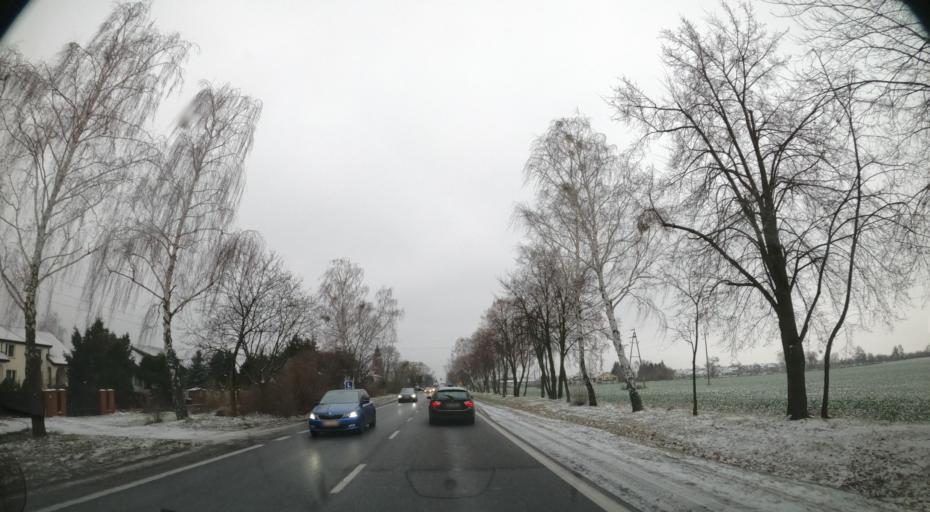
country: PL
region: Masovian Voivodeship
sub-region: Powiat plocki
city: Slupno
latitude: 52.5305
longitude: 19.7805
